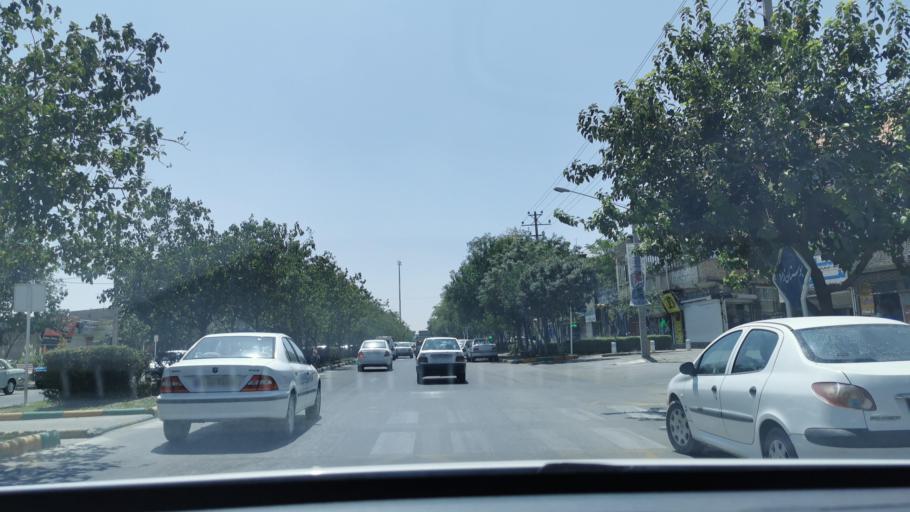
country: IR
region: Razavi Khorasan
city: Mashhad
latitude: 36.3451
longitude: 59.6262
